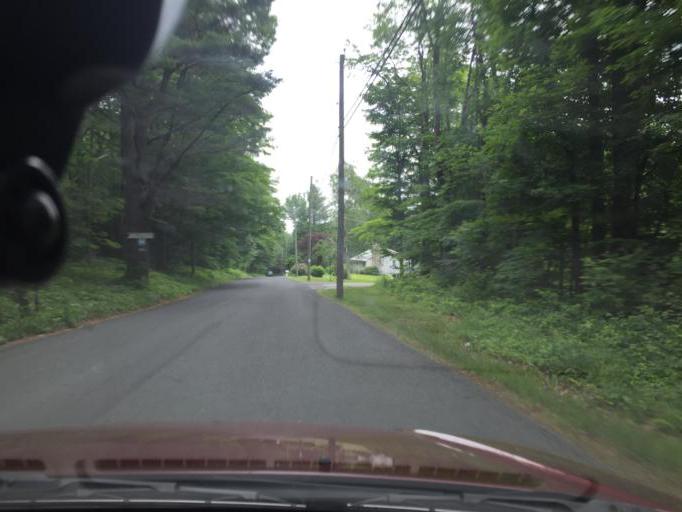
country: US
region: Connecticut
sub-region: Litchfield County
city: Litchfield
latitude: 41.7800
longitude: -73.2587
